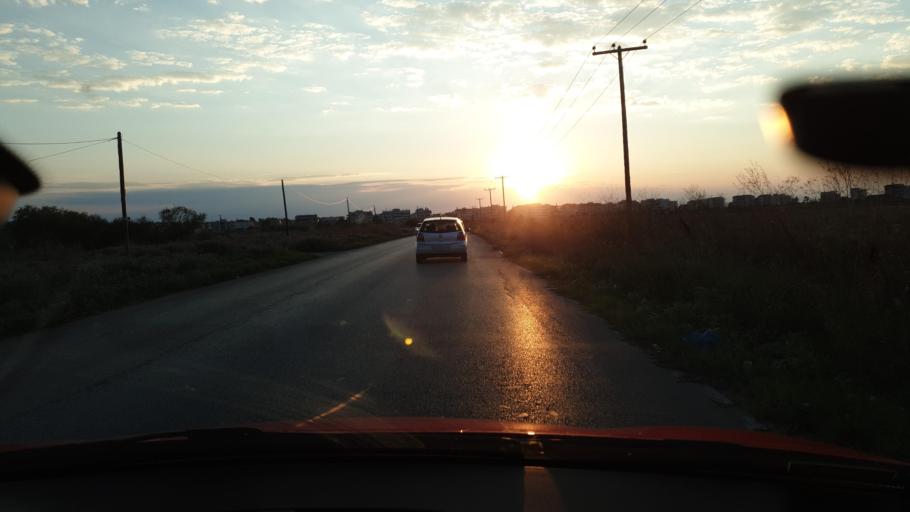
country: GR
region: Central Macedonia
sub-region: Nomos Thessalonikis
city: Peraia
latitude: 40.5078
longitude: 22.9450
